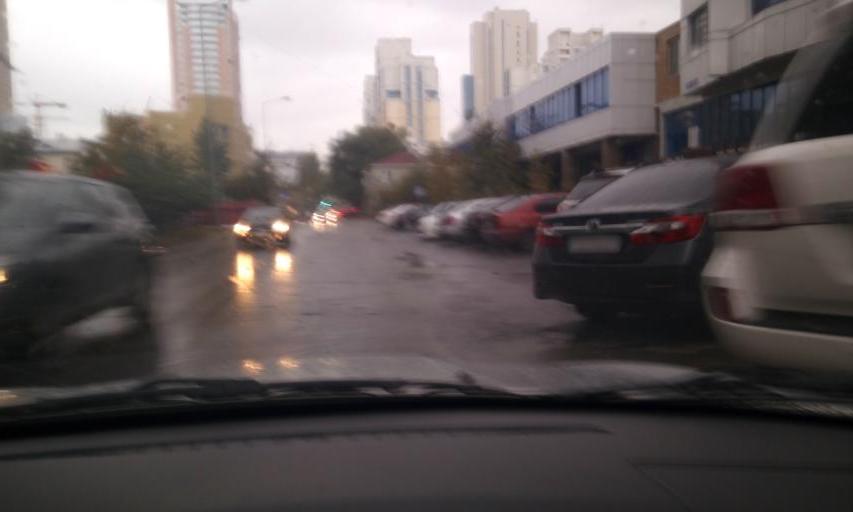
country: KZ
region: Astana Qalasy
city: Astana
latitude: 51.1618
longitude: 71.4325
